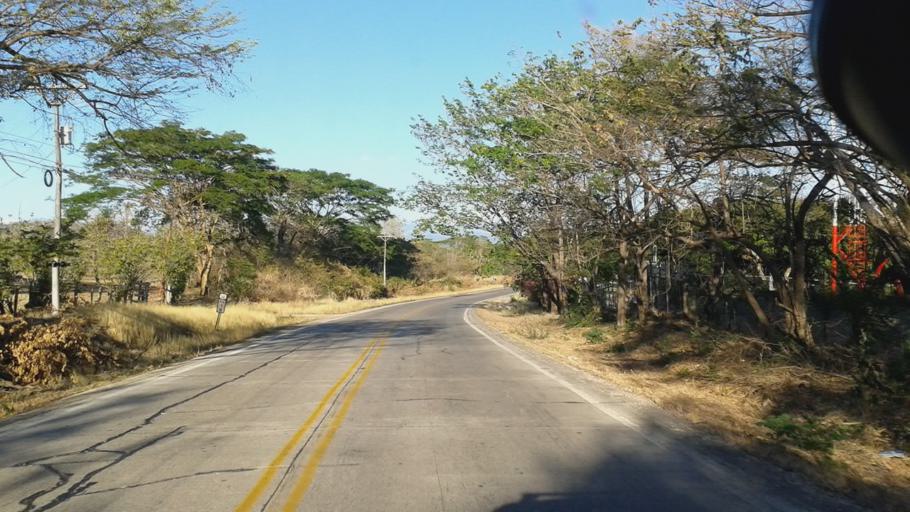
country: CR
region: Guanacaste
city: Nandayure
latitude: 10.2264
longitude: -85.1733
